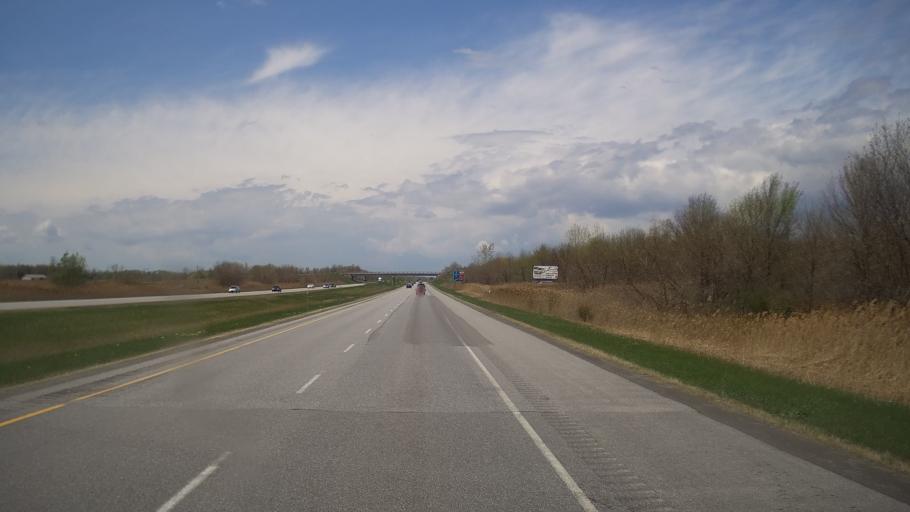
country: CA
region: Quebec
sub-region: Monteregie
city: Mercier
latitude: 45.3420
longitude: -73.6979
